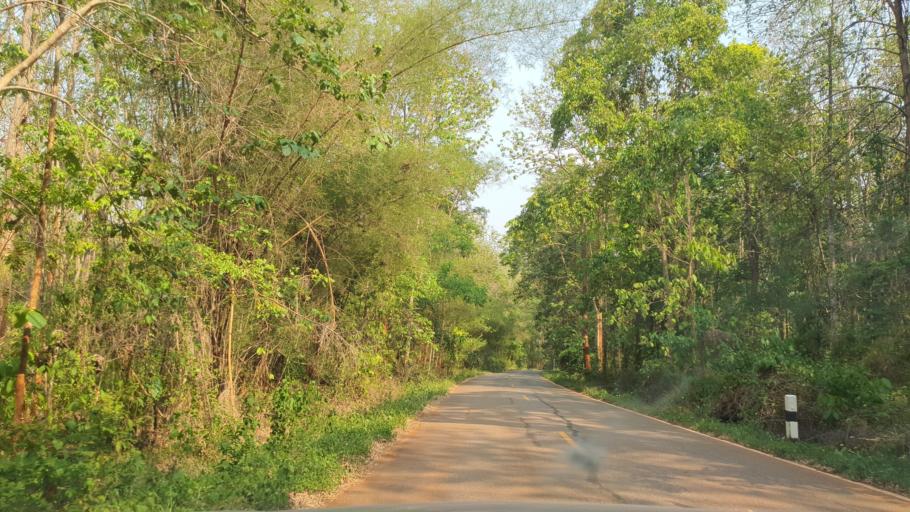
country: TH
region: Chiang Mai
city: San Sai
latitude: 19.0063
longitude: 99.1239
